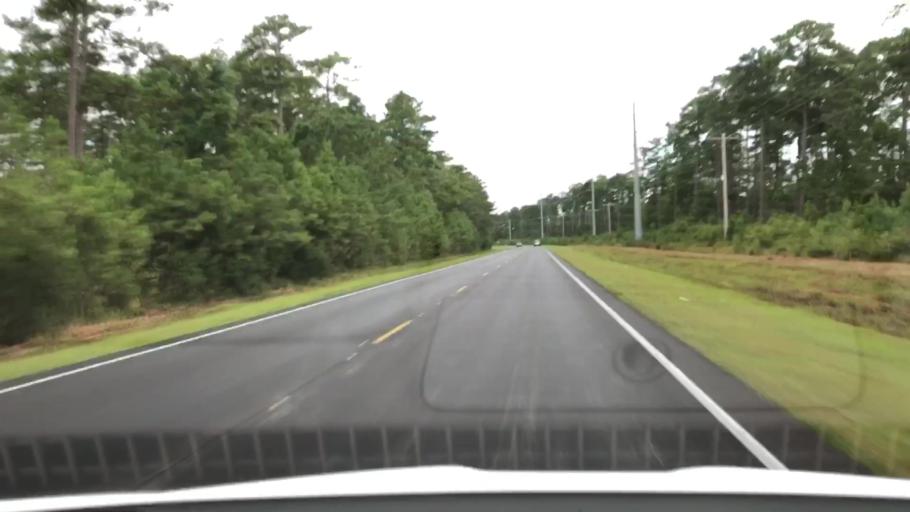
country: US
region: North Carolina
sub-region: Onslow County
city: Swansboro
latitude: 34.7845
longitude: -77.1155
